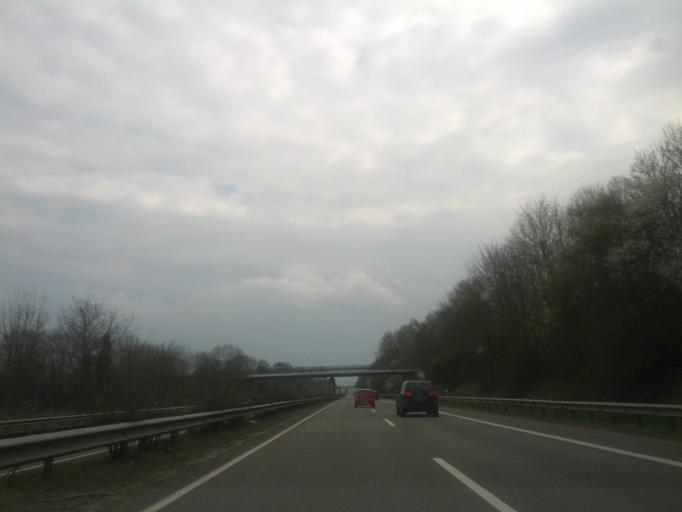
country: DE
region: Lower Saxony
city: Westerstede
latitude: 53.2707
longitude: 7.9233
